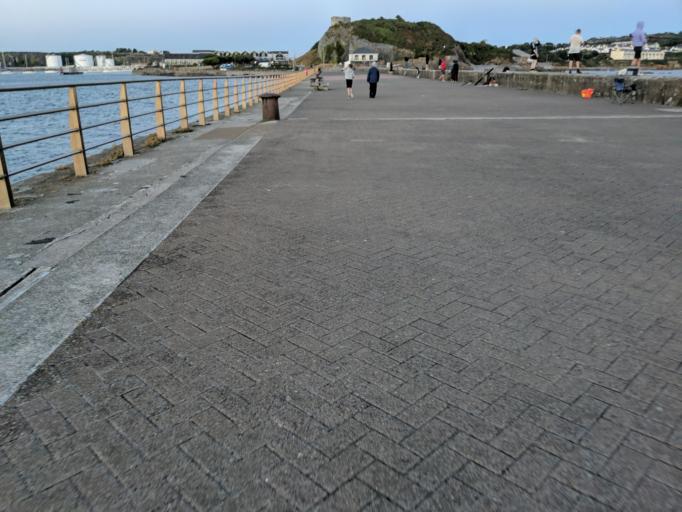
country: GB
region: England
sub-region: Plymouth
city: Plymouth
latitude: 50.3596
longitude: -4.1345
